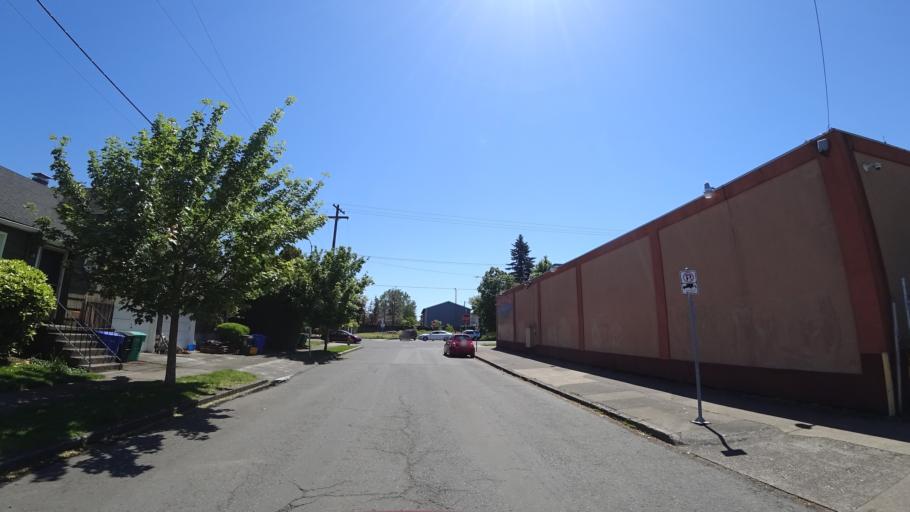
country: US
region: Oregon
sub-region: Multnomah County
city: Lents
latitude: 45.4980
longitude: -122.6060
